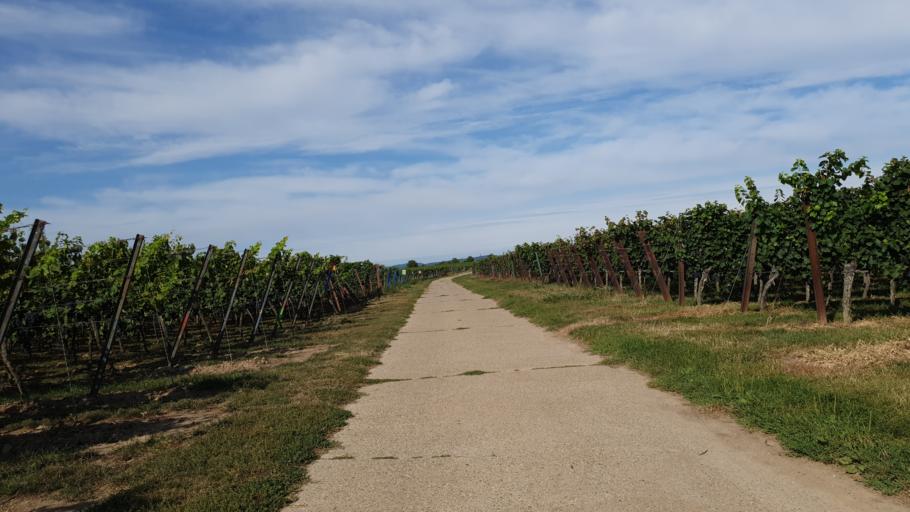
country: DE
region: Rheinland-Pfalz
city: Winden
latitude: 49.1183
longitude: 8.1117
